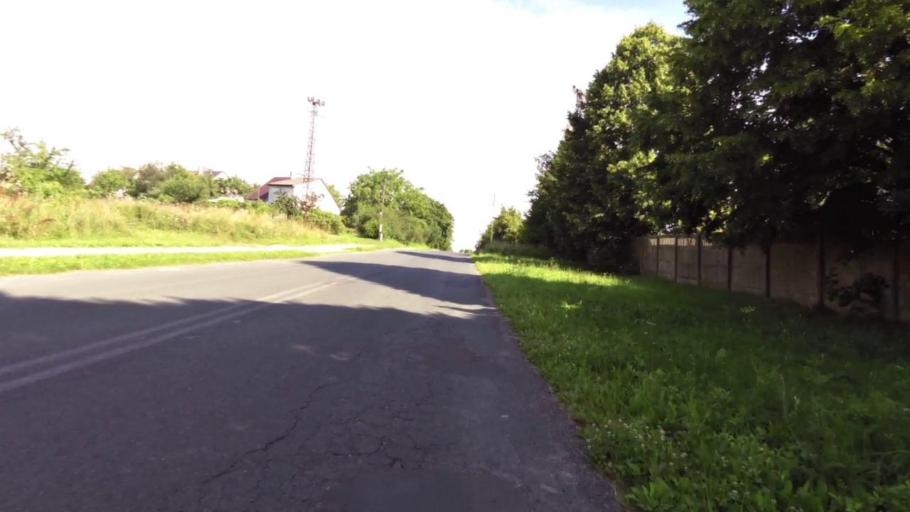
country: PL
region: West Pomeranian Voivodeship
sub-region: Powiat stargardzki
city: Dobrzany
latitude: 53.3829
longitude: 15.4352
